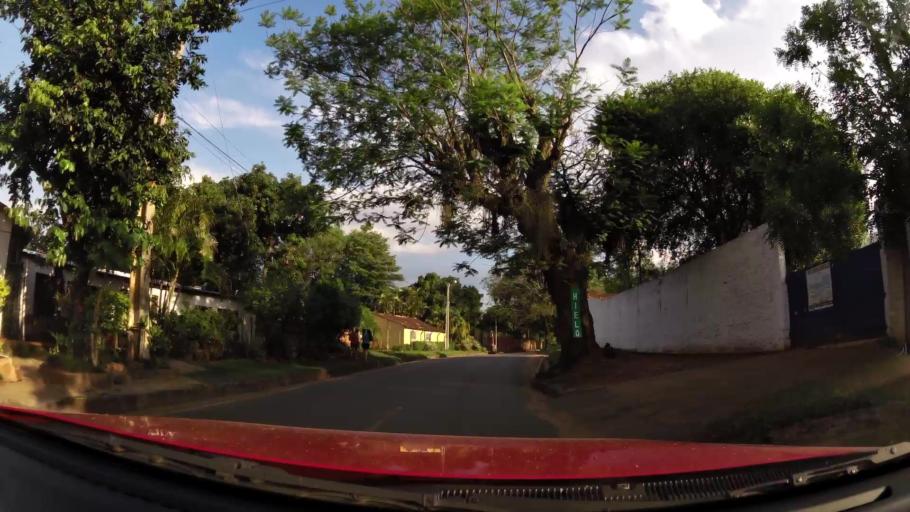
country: PY
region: Central
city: Fernando de la Mora
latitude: -25.3472
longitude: -57.5201
